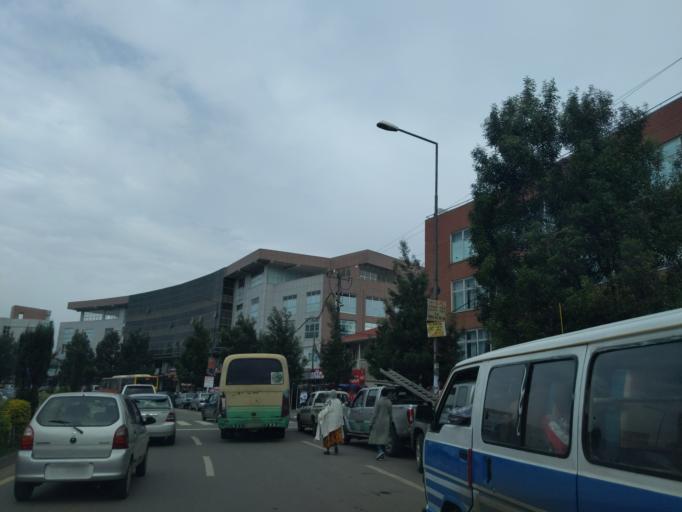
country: ET
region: Adis Abeba
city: Addis Ababa
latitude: 9.0322
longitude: 38.7648
